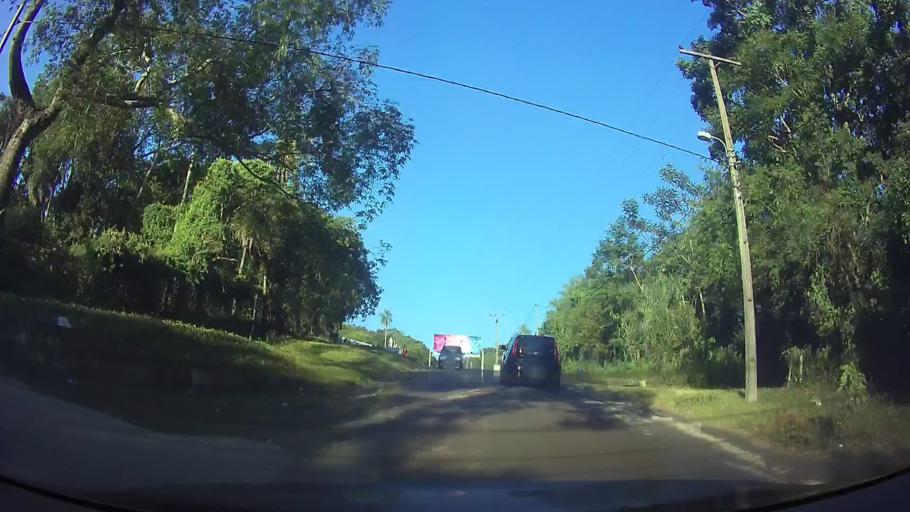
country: PY
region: Cordillera
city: San Bernardino
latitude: -25.3171
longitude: -57.2682
